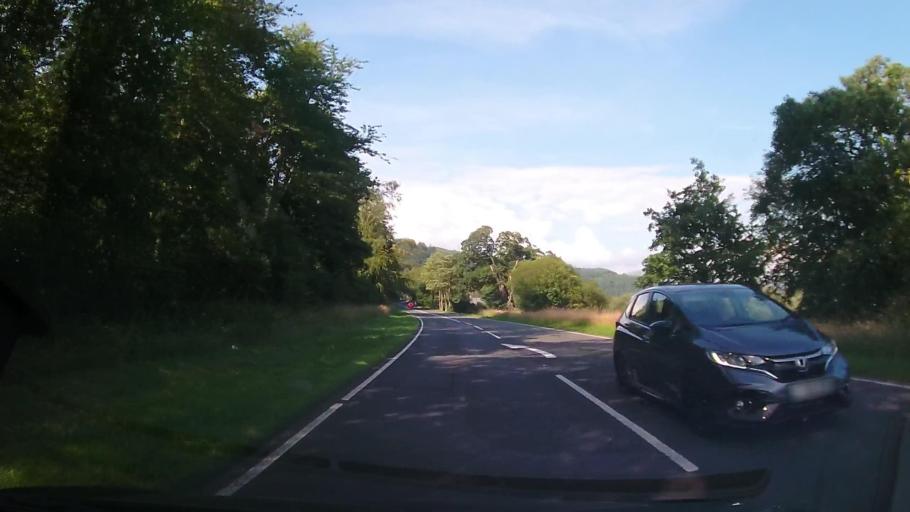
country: GB
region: Wales
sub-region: Gwynedd
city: Maentwrog
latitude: 52.9446
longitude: -4.0005
